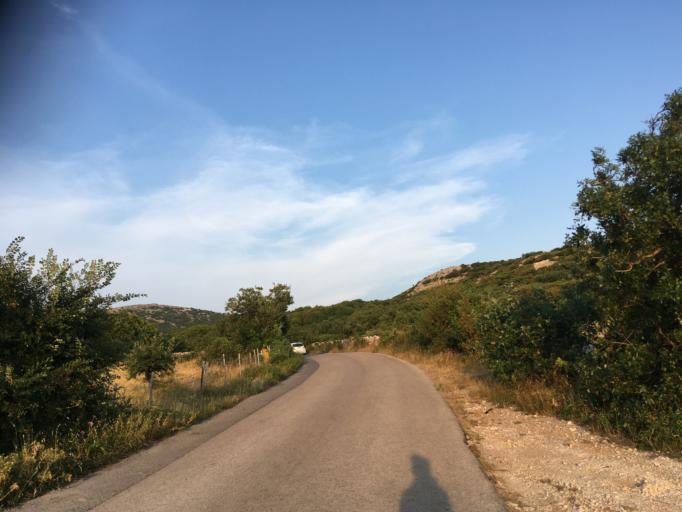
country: HR
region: Primorsko-Goranska
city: Punat
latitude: 44.9918
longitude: 14.6344
